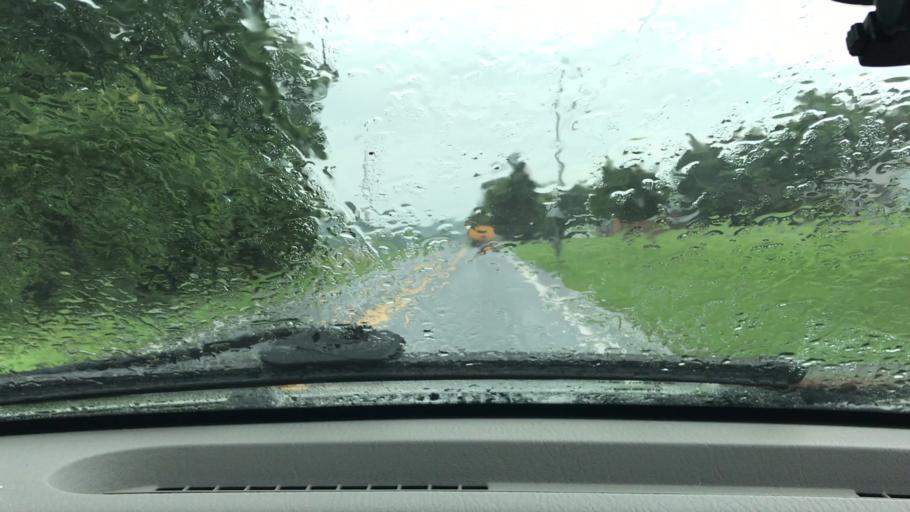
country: US
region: Pennsylvania
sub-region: Lancaster County
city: Elizabethtown
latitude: 40.1993
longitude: -76.6463
